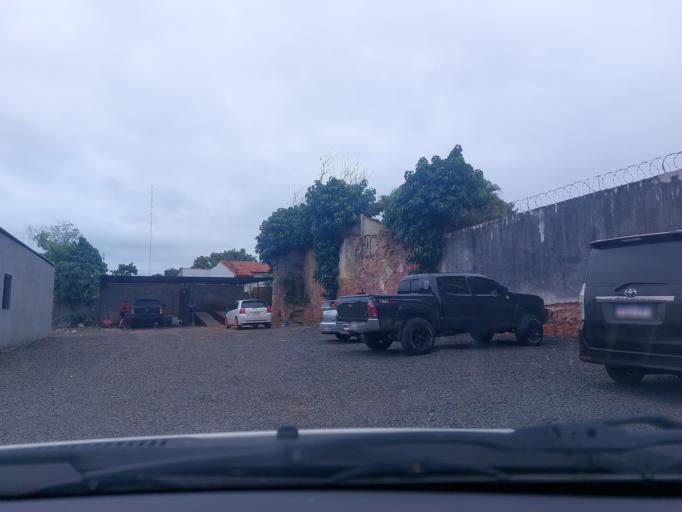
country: PY
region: San Pedro
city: Guayaybi
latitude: -24.6661
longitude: -56.4431
